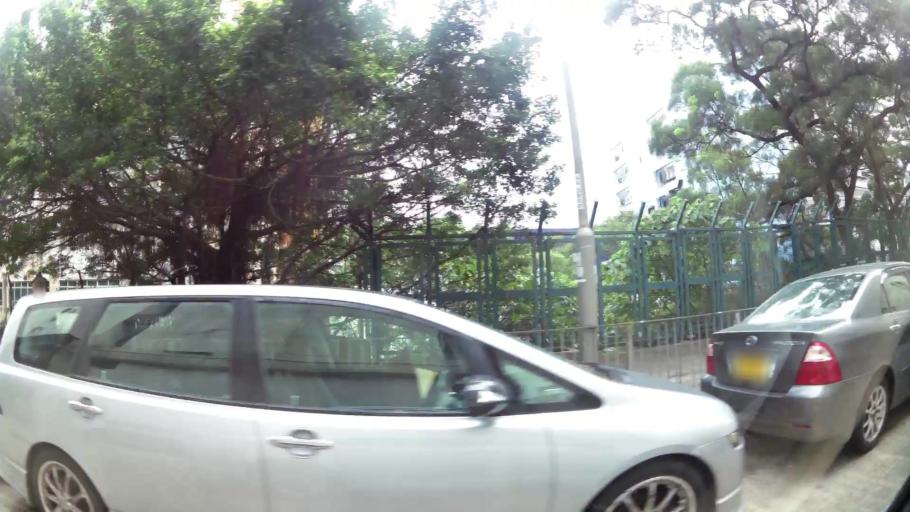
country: HK
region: Kowloon City
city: Kowloon
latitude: 22.2951
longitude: 114.2353
